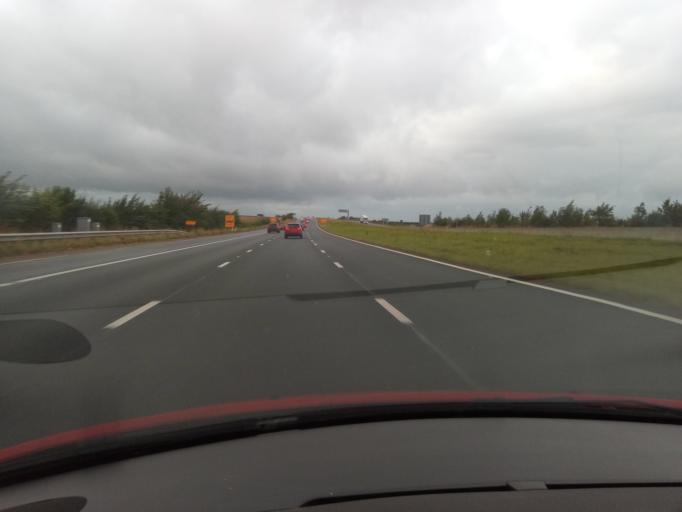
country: GB
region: England
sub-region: North Yorkshire
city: Ripon
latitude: 54.1682
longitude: -1.4508
